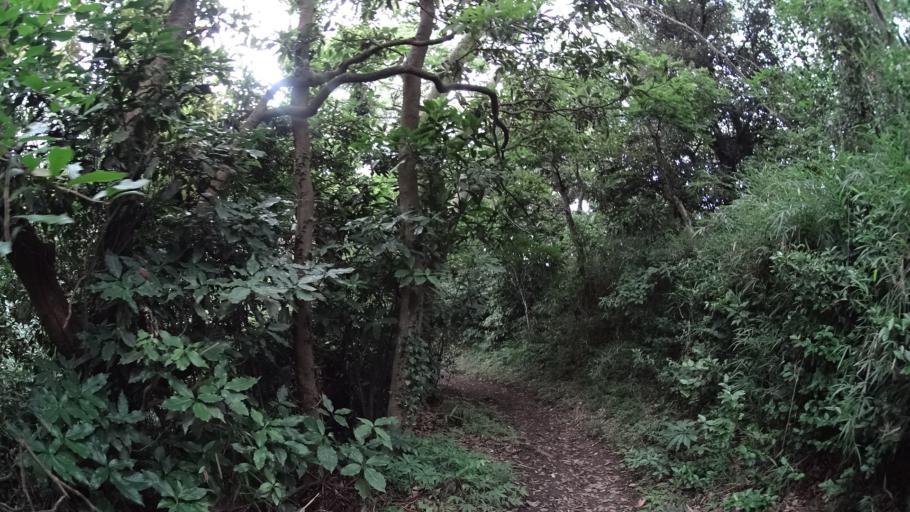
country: JP
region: Kanagawa
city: Yokosuka
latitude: 35.2204
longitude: 139.6604
